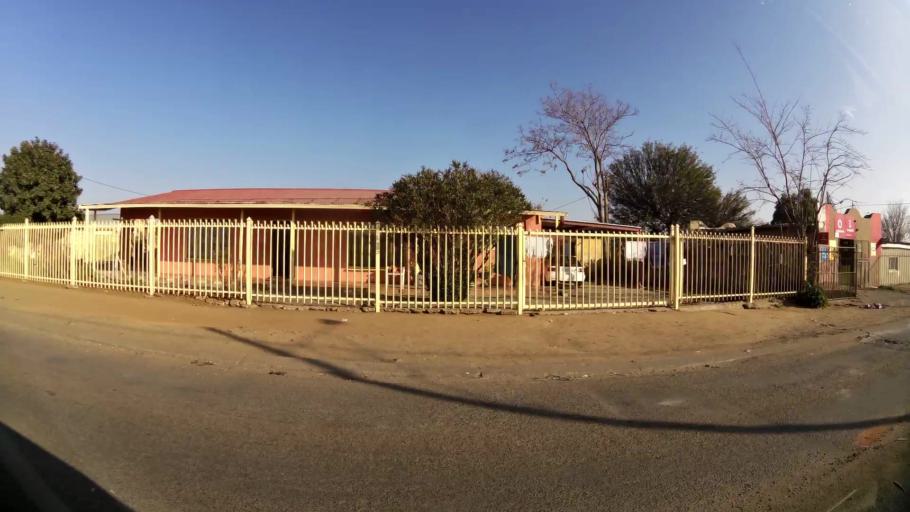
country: ZA
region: Orange Free State
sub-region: Mangaung Metropolitan Municipality
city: Bloemfontein
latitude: -29.1362
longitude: 26.2522
